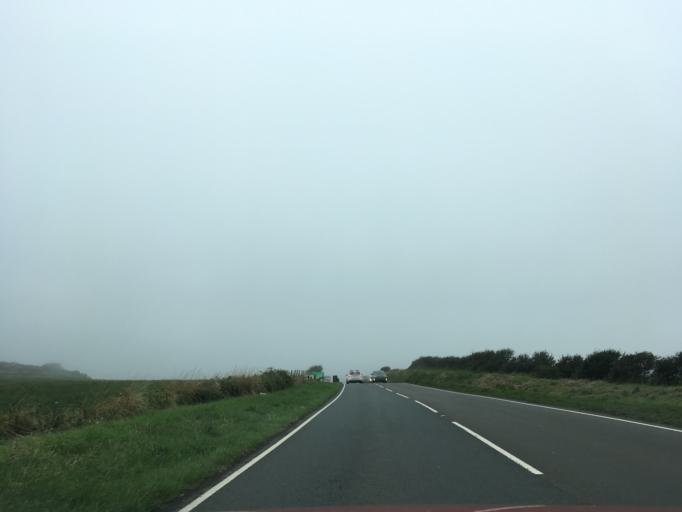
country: GB
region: Wales
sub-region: Pembrokeshire
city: Llanrhian
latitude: 51.8776
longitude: -5.1787
